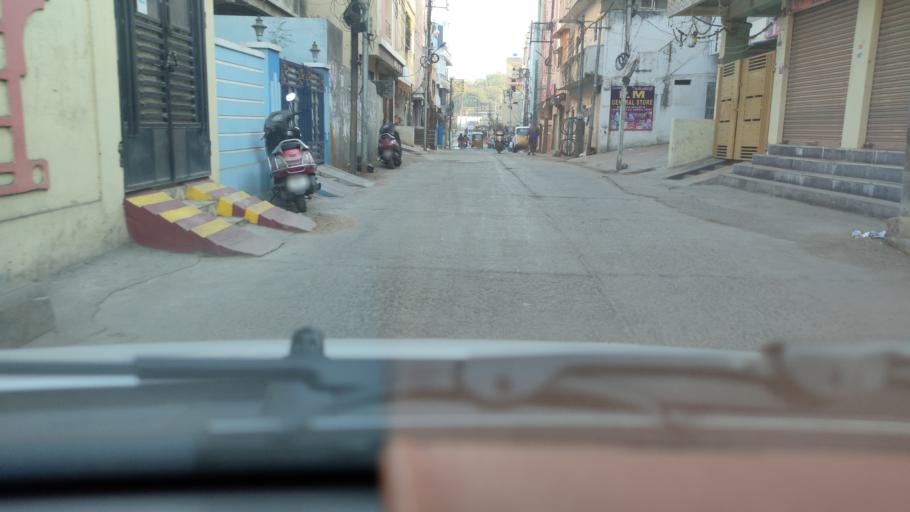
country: IN
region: Telangana
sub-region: Hyderabad
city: Malkajgiri
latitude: 17.4132
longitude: 78.5088
